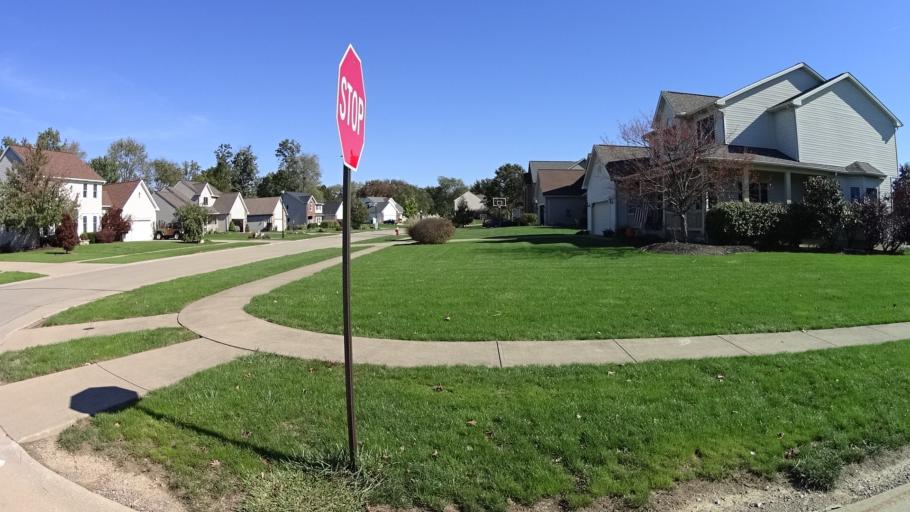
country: US
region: Ohio
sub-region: Lorain County
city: Amherst
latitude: 41.3878
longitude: -82.2221
